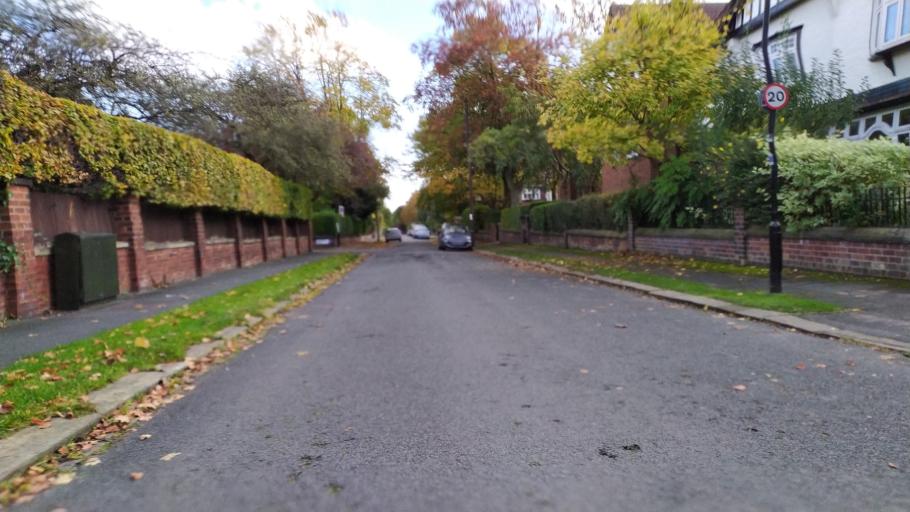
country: GB
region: England
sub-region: City and Borough of Leeds
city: Horsforth
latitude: 53.8335
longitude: -1.5979
